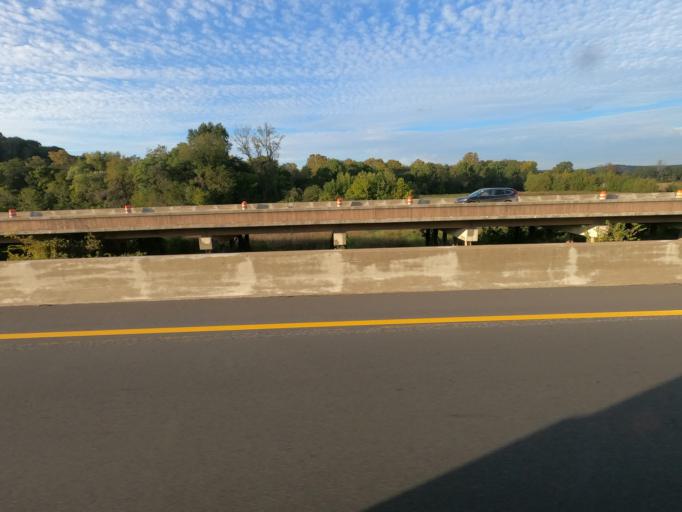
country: US
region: Tennessee
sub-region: Humphreys County
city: New Johnsonville
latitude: 35.8816
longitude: -87.8299
